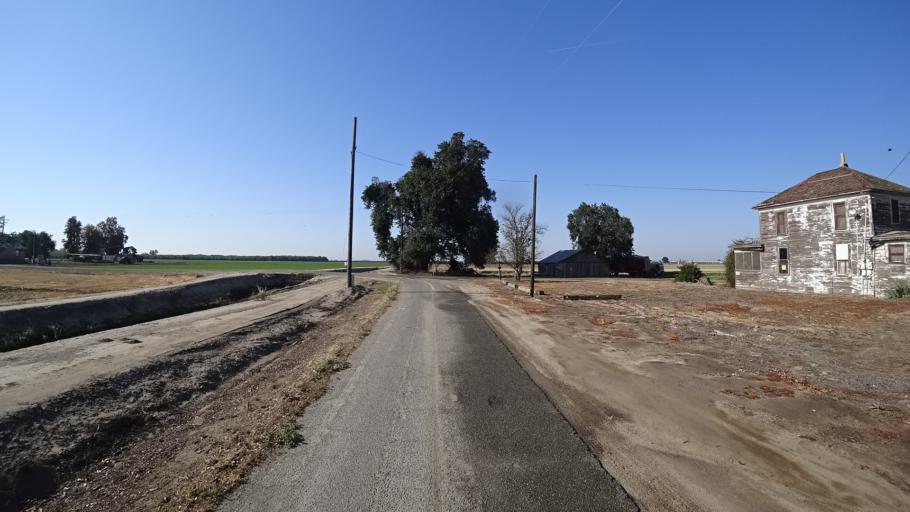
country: US
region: California
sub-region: Fresno County
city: Laton
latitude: 36.3917
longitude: -119.7181
